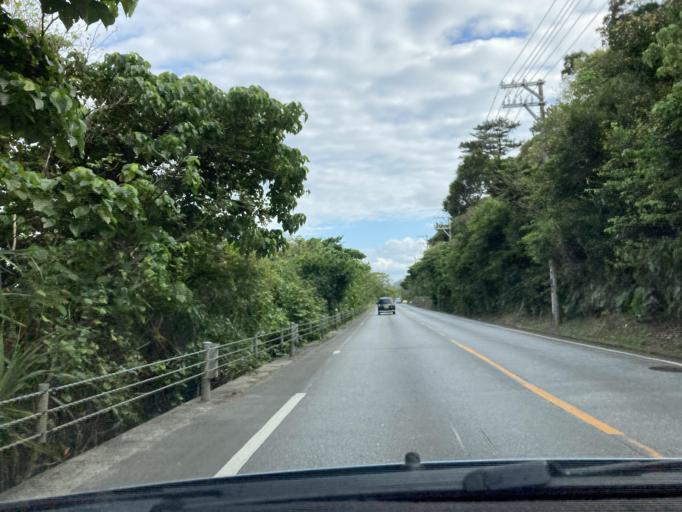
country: JP
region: Okinawa
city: Nago
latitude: 26.6436
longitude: 127.9976
